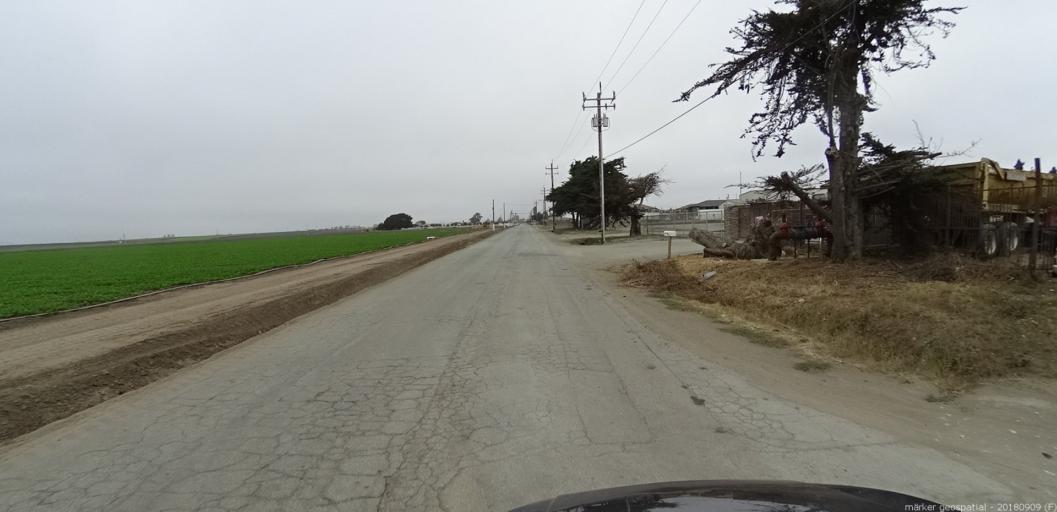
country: US
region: California
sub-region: Monterey County
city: Boronda
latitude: 36.6928
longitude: -121.6799
